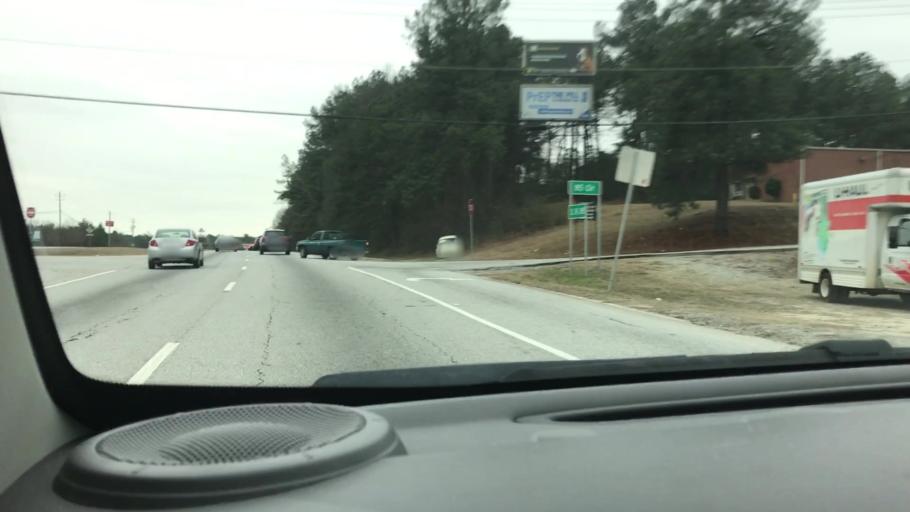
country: US
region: Georgia
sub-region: Clayton County
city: Forest Park
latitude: 33.6223
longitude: -84.4027
